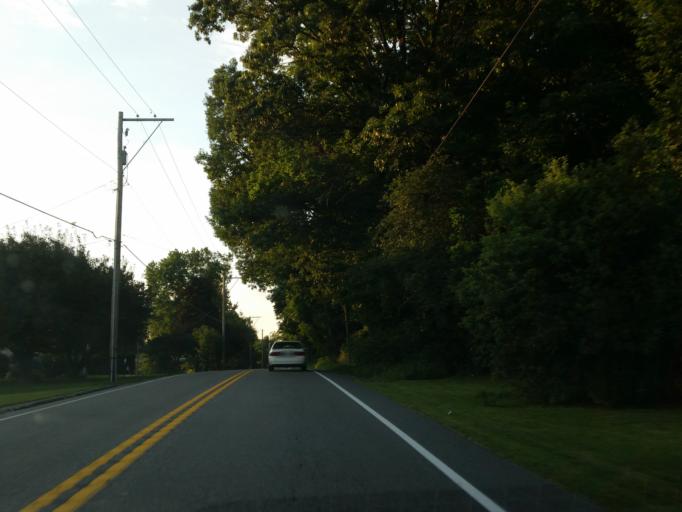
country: US
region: Pennsylvania
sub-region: Lancaster County
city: Swartzville
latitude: 40.2415
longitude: -76.0827
